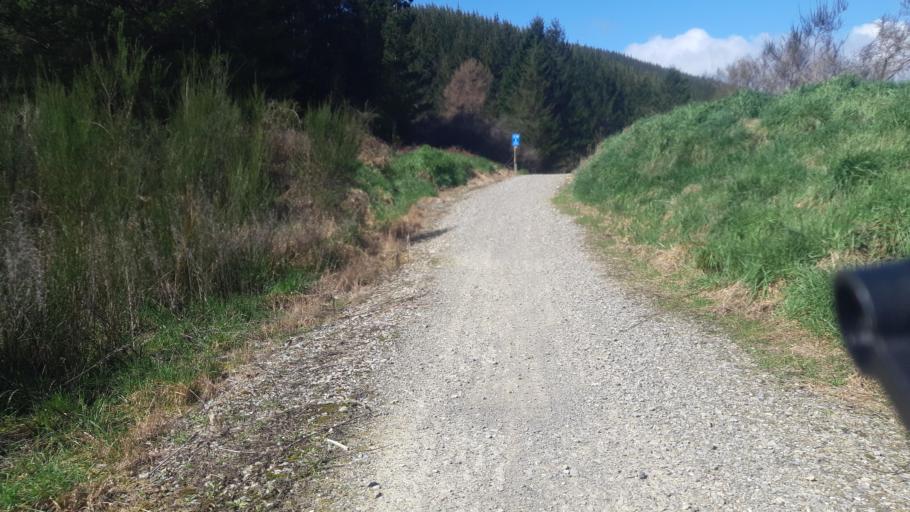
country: NZ
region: Tasman
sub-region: Tasman District
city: Wakefield
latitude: -41.4887
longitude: 172.8933
